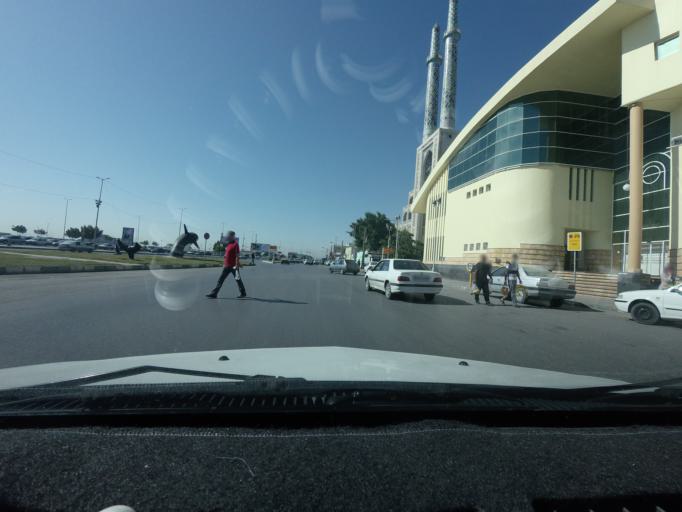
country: IR
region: Hormozgan
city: Bandar 'Abbas
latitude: 27.1790
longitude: 56.2835
